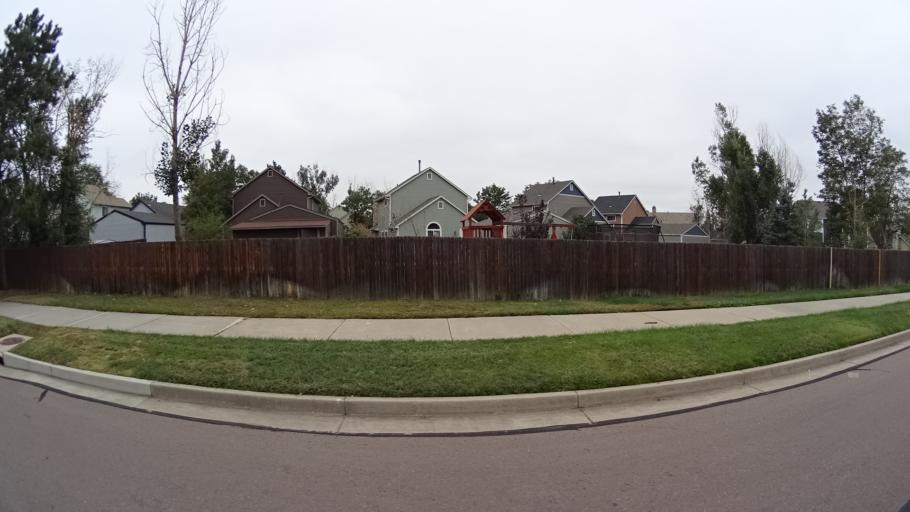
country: US
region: Colorado
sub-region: El Paso County
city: Cimarron Hills
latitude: 38.9052
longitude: -104.7072
